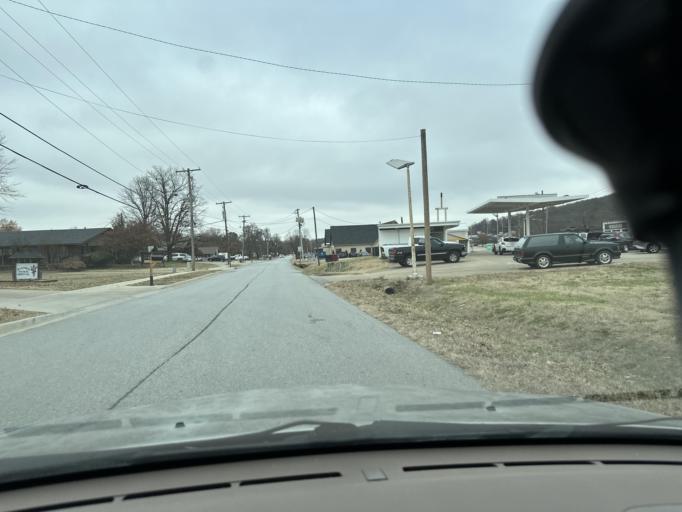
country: US
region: Arkansas
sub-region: Washington County
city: Fayetteville
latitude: 36.0864
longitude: -94.1554
